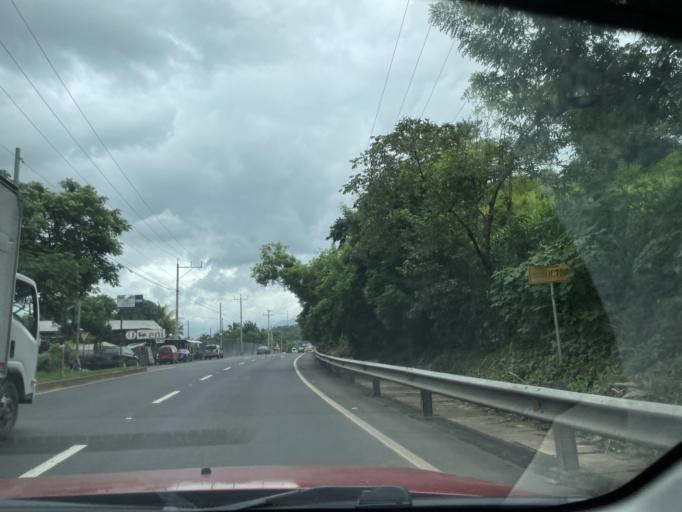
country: SV
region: Sonsonate
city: Armenia
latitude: 13.7415
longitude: -89.4315
